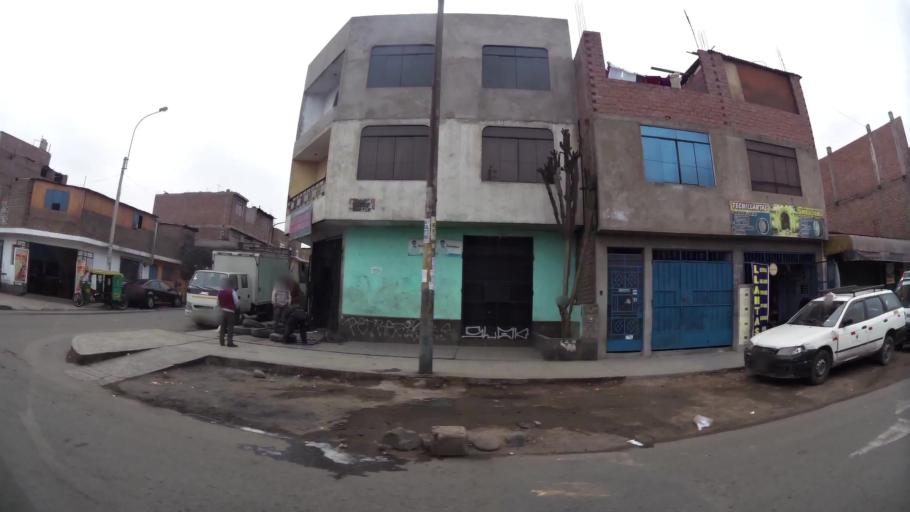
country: PE
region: Lima
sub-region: Lima
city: Vitarte
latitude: -12.0395
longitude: -76.9612
